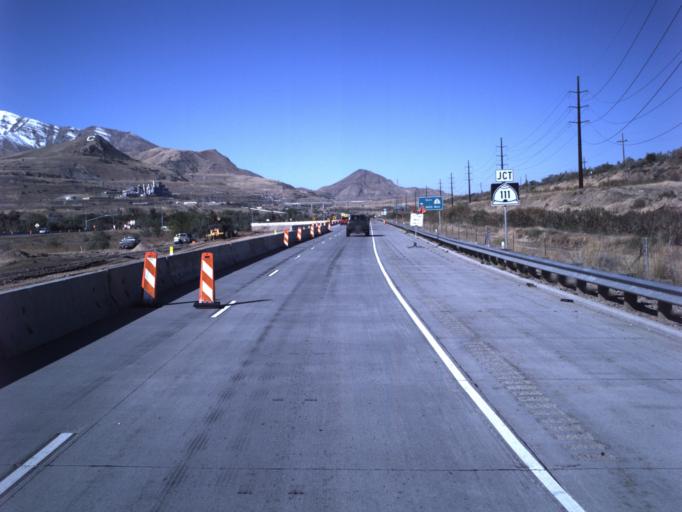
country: US
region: Utah
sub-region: Salt Lake County
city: Magna
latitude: 40.7182
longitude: -112.0865
